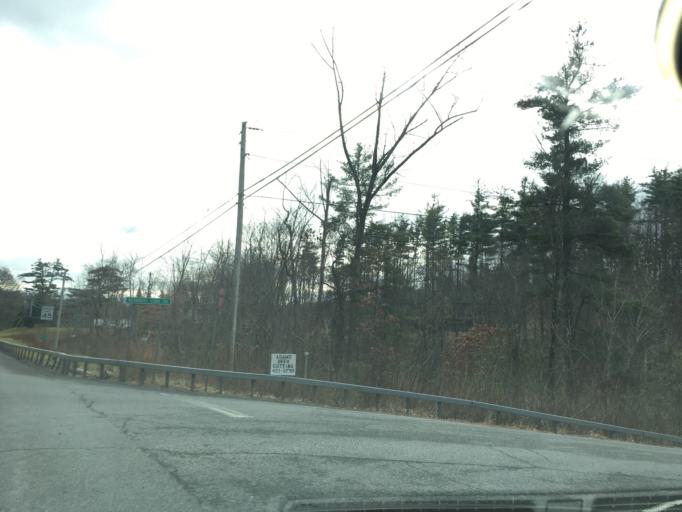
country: US
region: New York
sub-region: Rensselaer County
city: Averill Park
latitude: 42.6046
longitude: -73.5206
